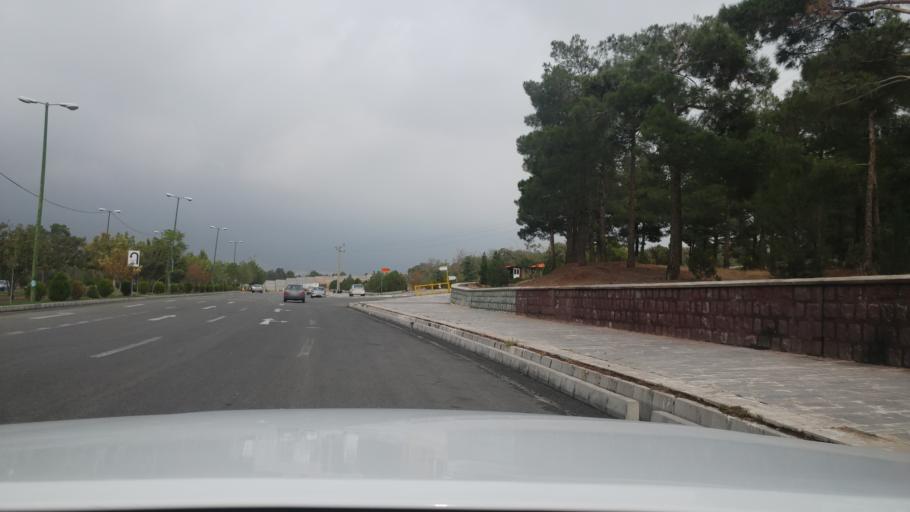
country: IR
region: Tehran
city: Shahr-e Qods
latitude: 35.7267
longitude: 51.2194
